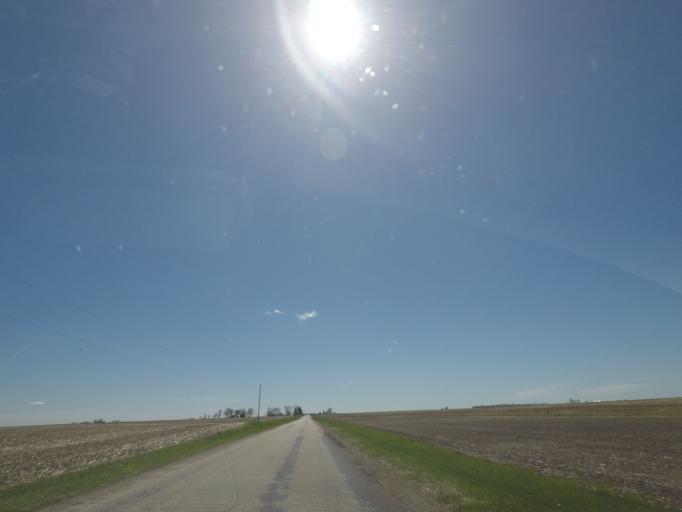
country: US
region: Illinois
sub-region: Logan County
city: Atlanta
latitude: 40.1772
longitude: -89.1938
